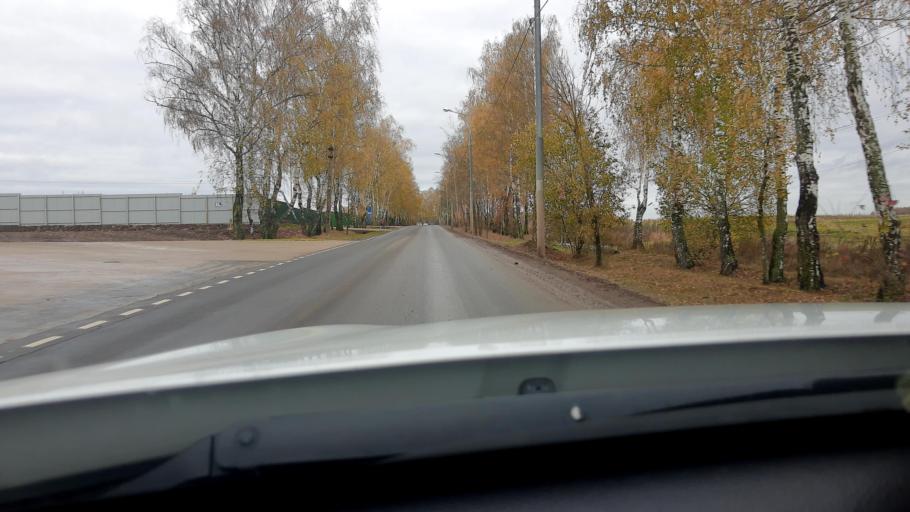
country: RU
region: Moskovskaya
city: Annino
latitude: 55.5686
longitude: 37.2358
